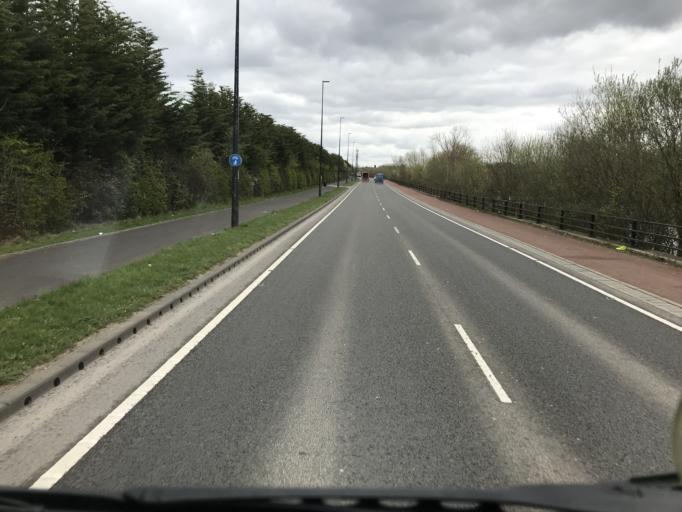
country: GB
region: England
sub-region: Trafford
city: Partington
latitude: 53.4191
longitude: -2.4428
